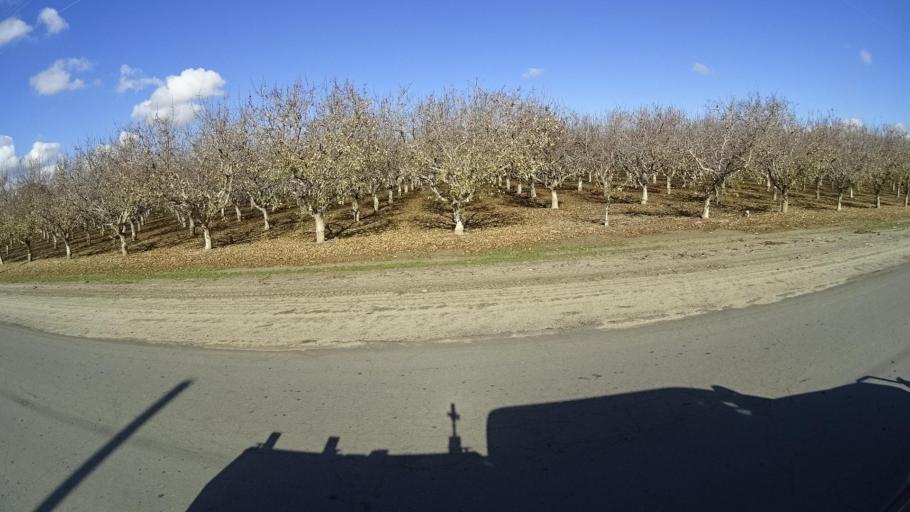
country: US
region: California
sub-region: Kern County
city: McFarland
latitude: 35.6886
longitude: -119.2977
